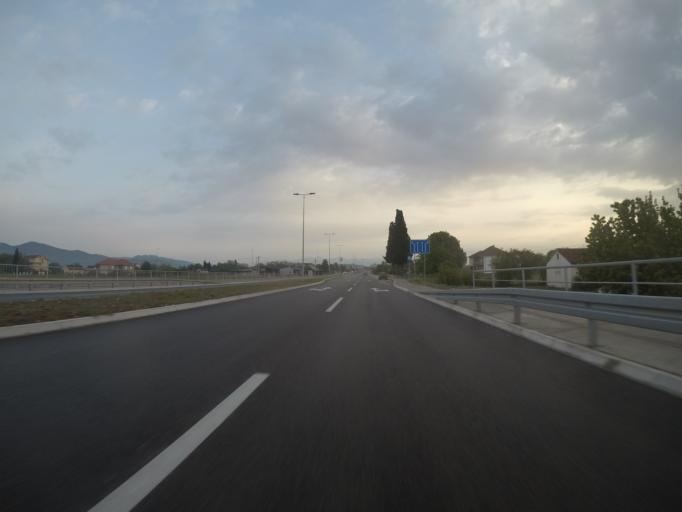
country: ME
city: Mojanovici
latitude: 42.3508
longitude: 19.2226
